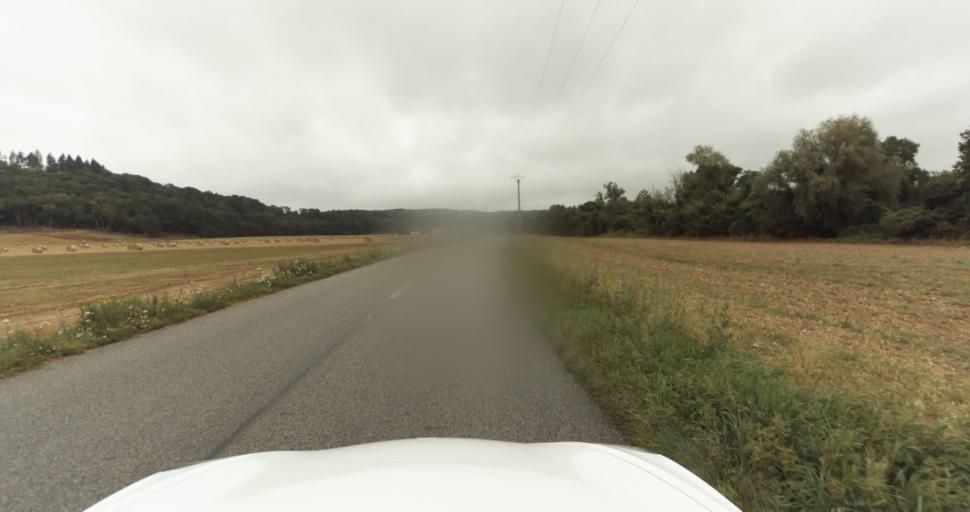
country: FR
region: Haute-Normandie
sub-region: Departement de l'Eure
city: Normanville
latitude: 49.0798
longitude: 1.1433
